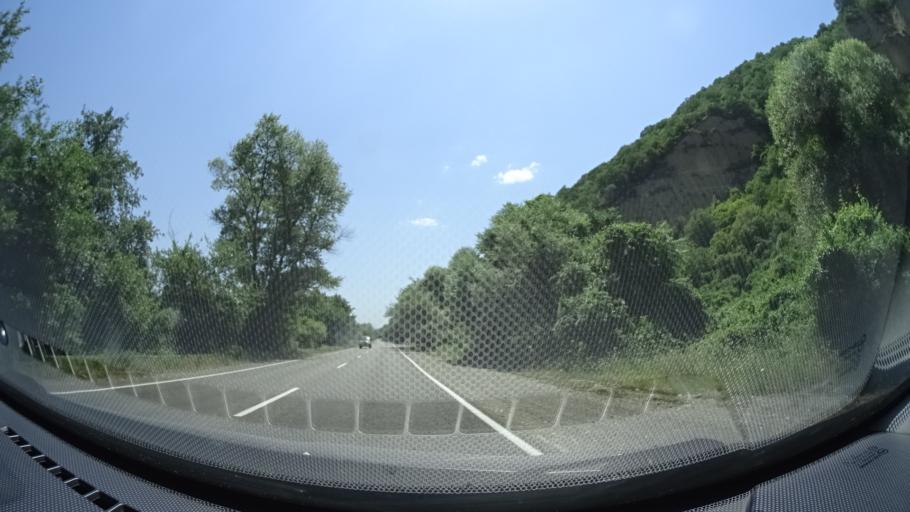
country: GE
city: Zhinvali
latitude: 42.0419
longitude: 44.7453
